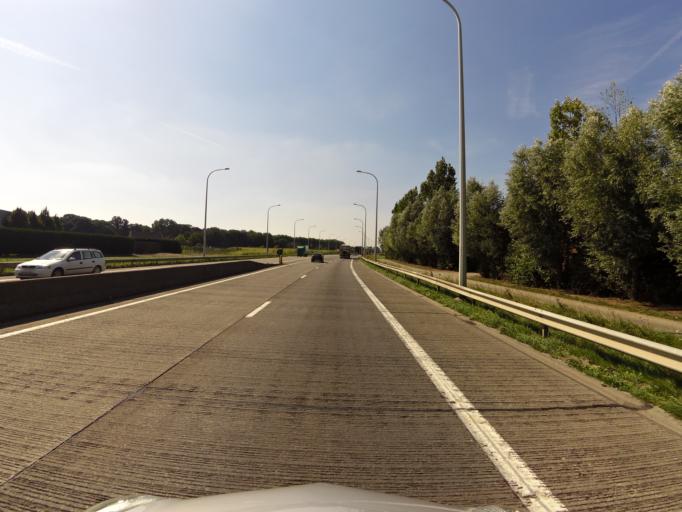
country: BE
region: Flanders
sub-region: Provincie West-Vlaanderen
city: Pittem
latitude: 50.9858
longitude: 3.2568
